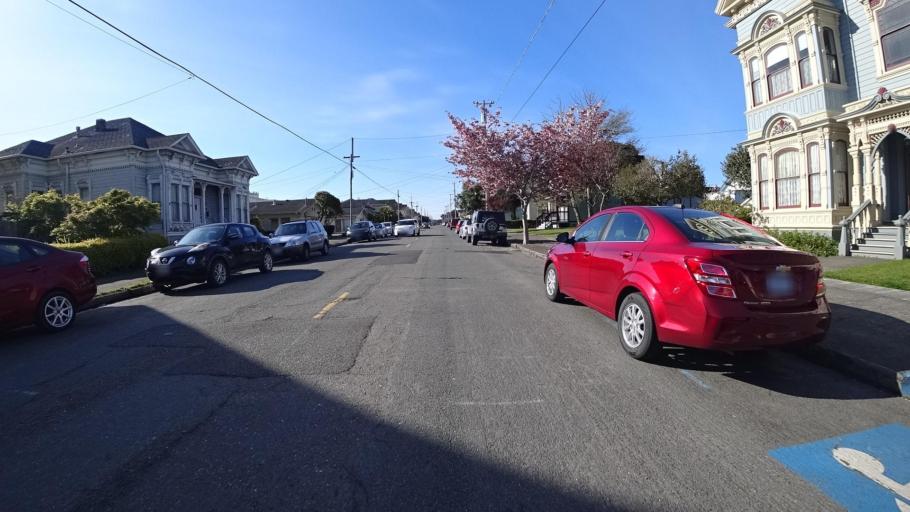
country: US
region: California
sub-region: Humboldt County
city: Eureka
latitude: 40.7987
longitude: -124.1642
